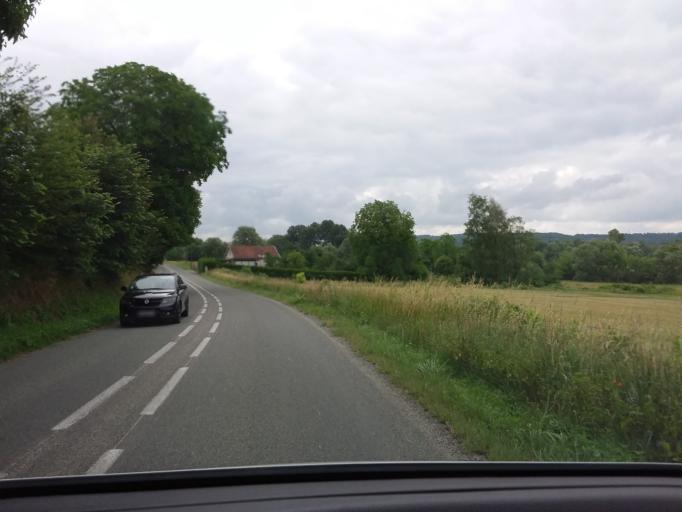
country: FR
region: Picardie
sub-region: Departement de l'Aisne
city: Vailly-sur-Aisne
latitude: 49.4026
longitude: 3.5639
